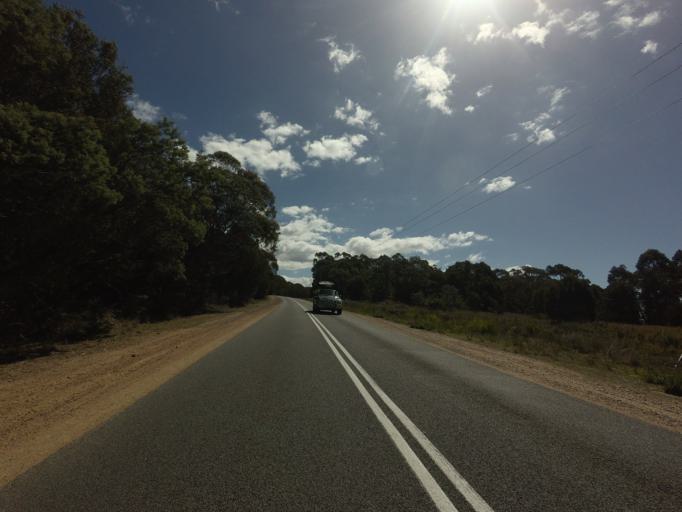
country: AU
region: Tasmania
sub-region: Break O'Day
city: St Helens
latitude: -41.6827
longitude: 148.2814
